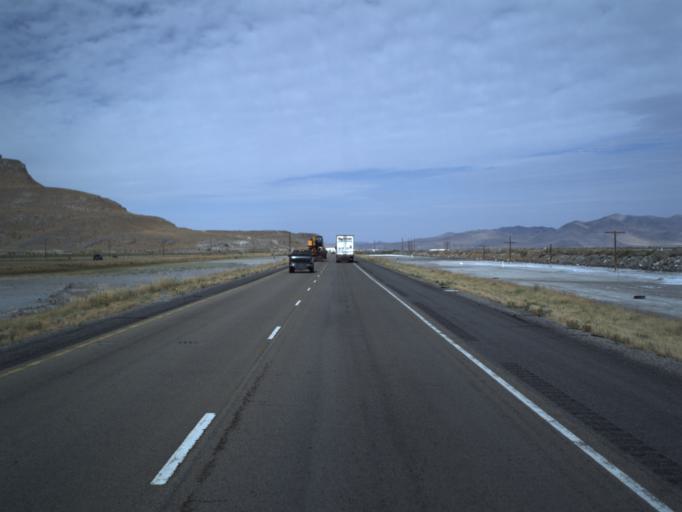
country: US
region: Utah
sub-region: Tooele County
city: Grantsville
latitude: 40.7382
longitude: -112.6152
